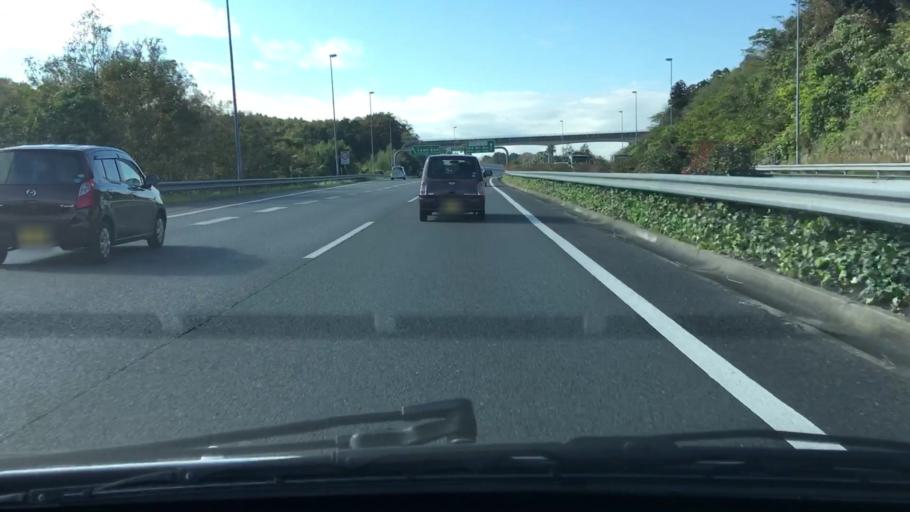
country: JP
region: Chiba
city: Kisarazu
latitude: 35.3573
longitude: 139.9529
